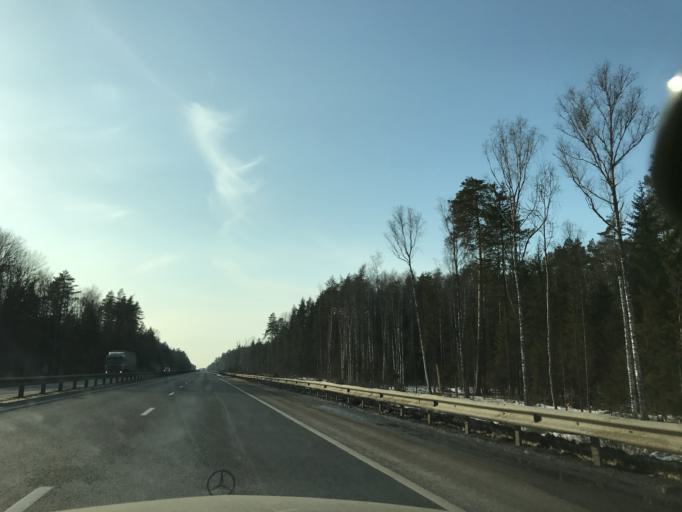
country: RU
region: Vladimir
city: Mstera
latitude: 56.2347
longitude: 41.8580
